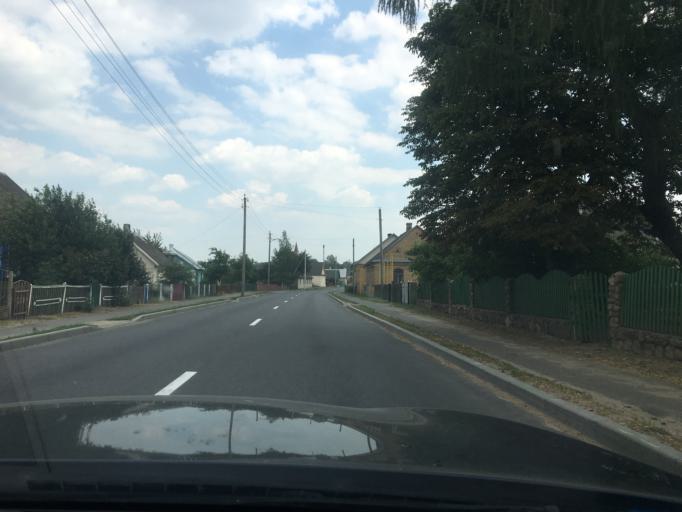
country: BY
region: Brest
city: Ruzhany
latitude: 52.8672
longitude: 24.8801
